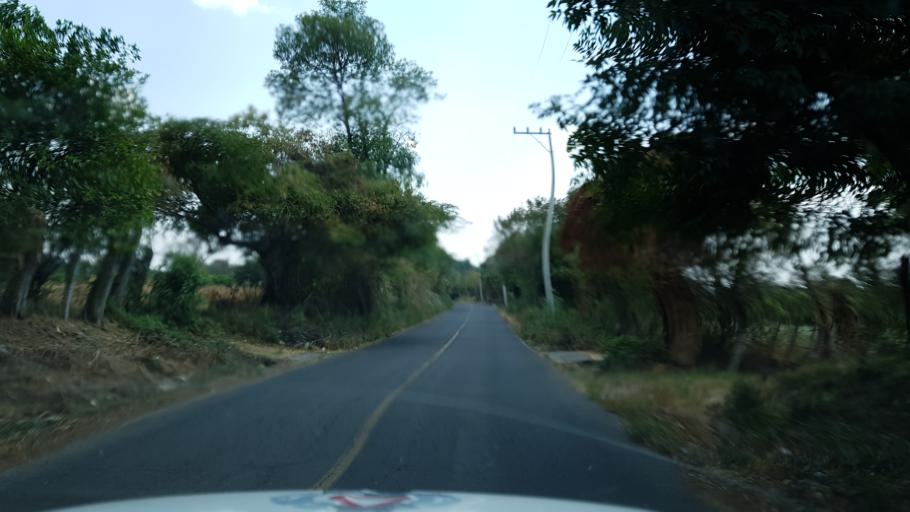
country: MX
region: Morelos
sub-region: Yecapixtla
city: Texcala
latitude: 18.9134
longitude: -98.8077
